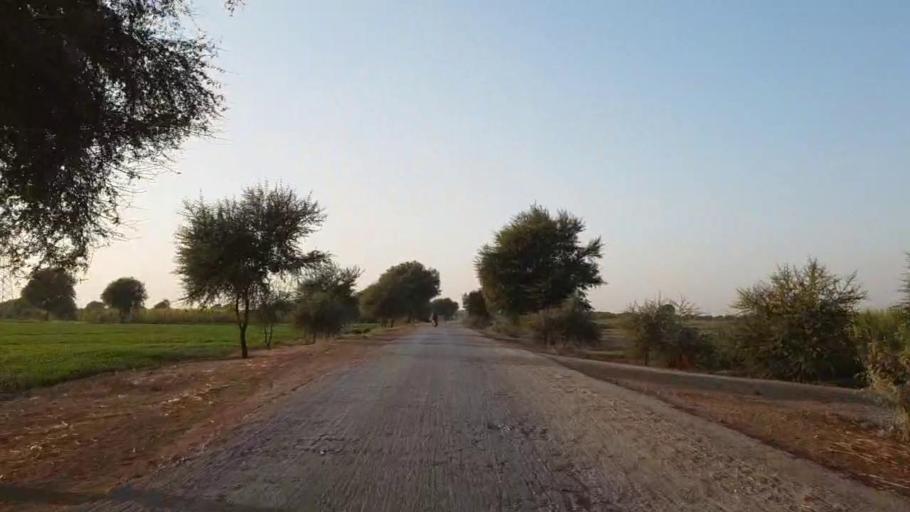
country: PK
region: Sindh
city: Chambar
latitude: 25.2288
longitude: 68.7091
